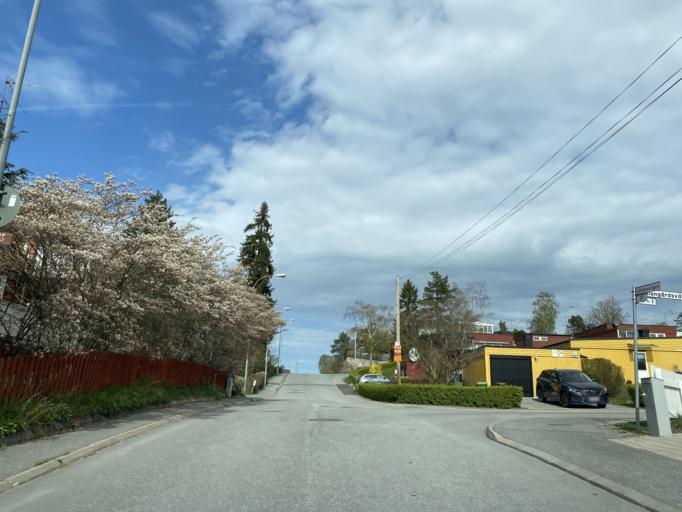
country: SE
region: Stockholm
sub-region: Sollentuna Kommun
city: Sollentuna
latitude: 59.4192
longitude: 17.9442
